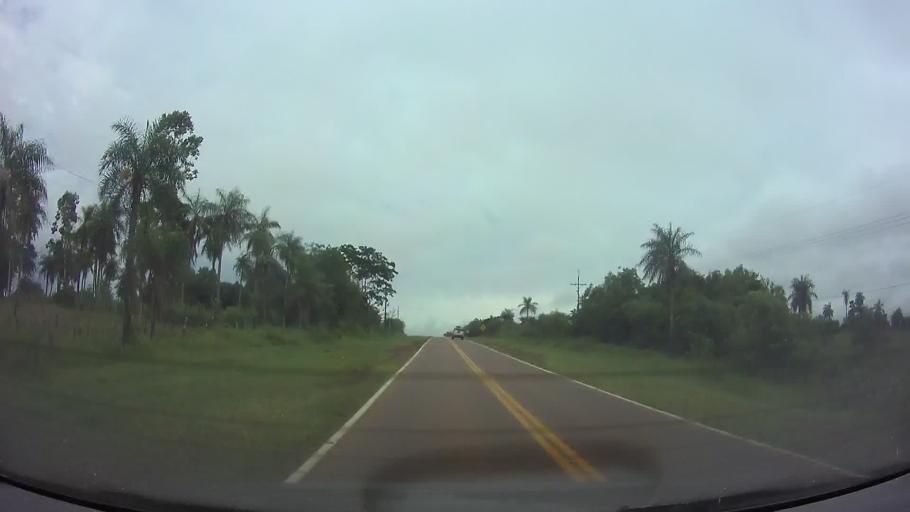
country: PY
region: Paraguari
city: Acahay
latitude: -25.8761
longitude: -57.1240
